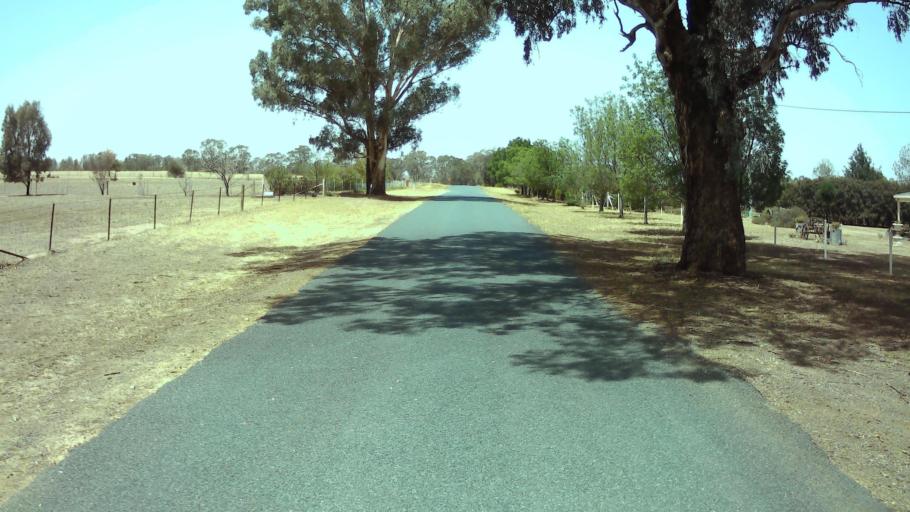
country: AU
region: New South Wales
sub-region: Weddin
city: Grenfell
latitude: -33.9079
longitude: 148.1509
